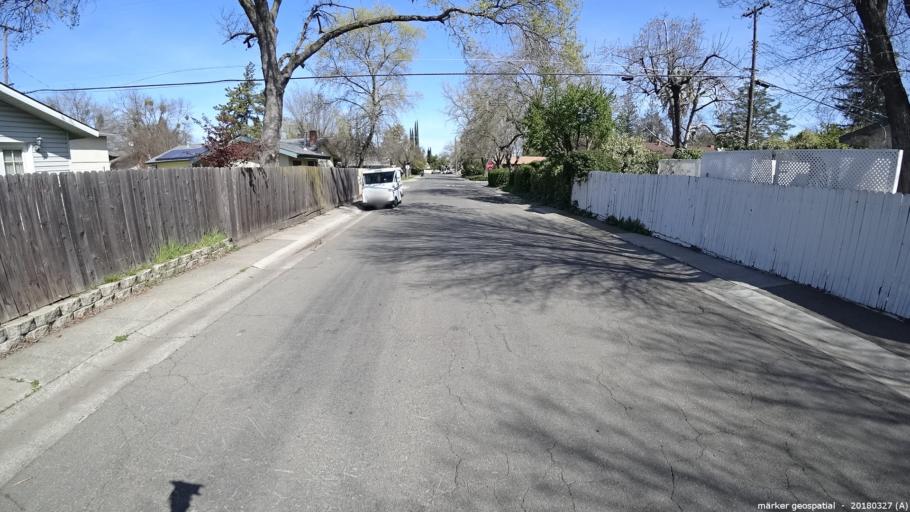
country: US
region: California
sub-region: Sacramento County
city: Rosemont
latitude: 38.5534
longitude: -121.3680
